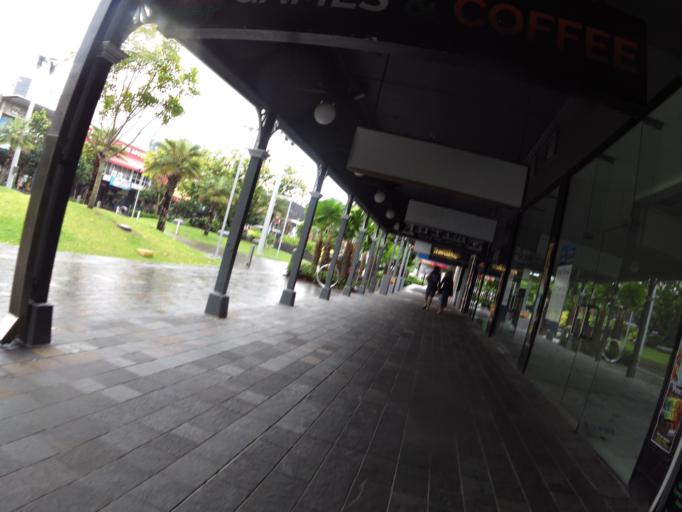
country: AU
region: Queensland
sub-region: Cairns
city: Cairns
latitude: -16.9214
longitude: 145.7759
